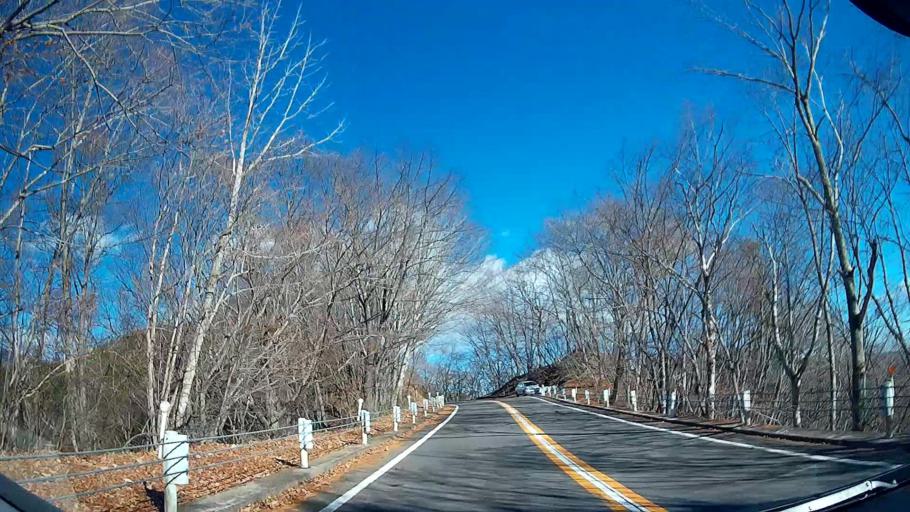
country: JP
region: Yamanashi
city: Uenohara
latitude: 35.7548
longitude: 139.0426
